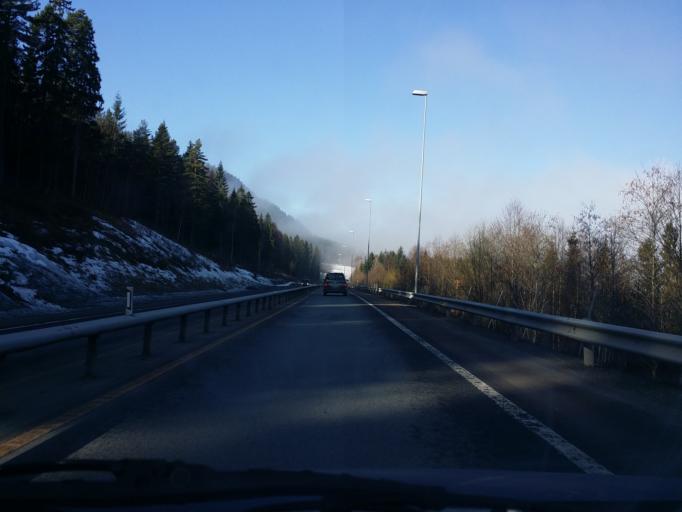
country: NO
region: Buskerud
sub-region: Nedre Eiker
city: Mjondalen
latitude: 59.7428
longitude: 10.0818
